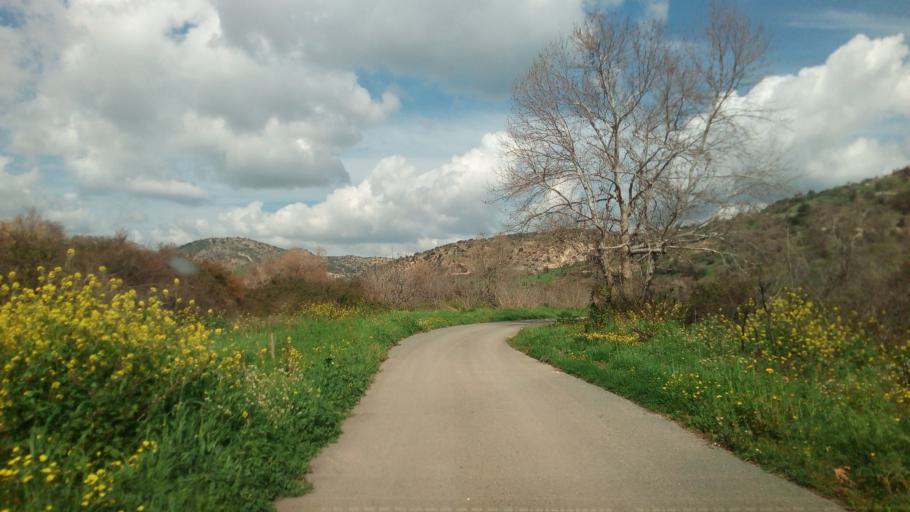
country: CY
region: Pafos
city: Mesogi
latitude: 34.8044
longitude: 32.5308
